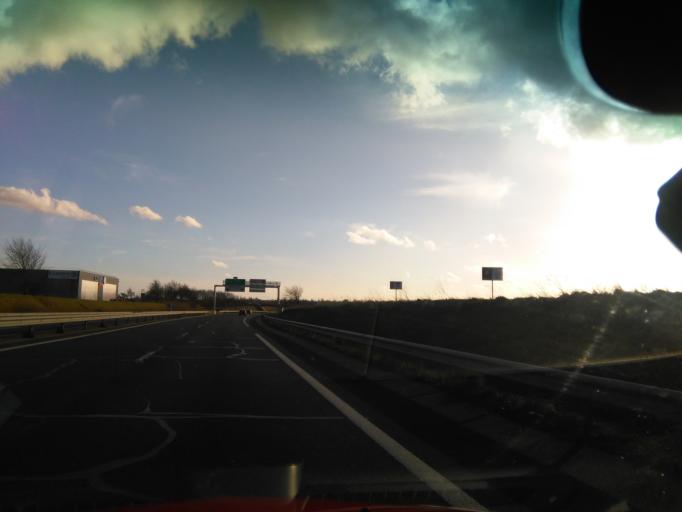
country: FR
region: Lower Normandy
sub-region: Departement du Calvados
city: Falaise
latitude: 48.9163
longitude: -0.2067
